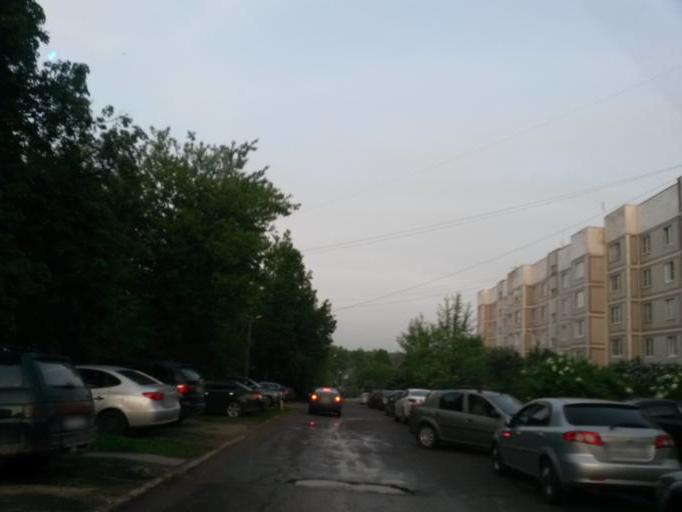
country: RU
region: Moskovskaya
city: Lyubuchany
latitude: 55.2408
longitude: 37.5424
